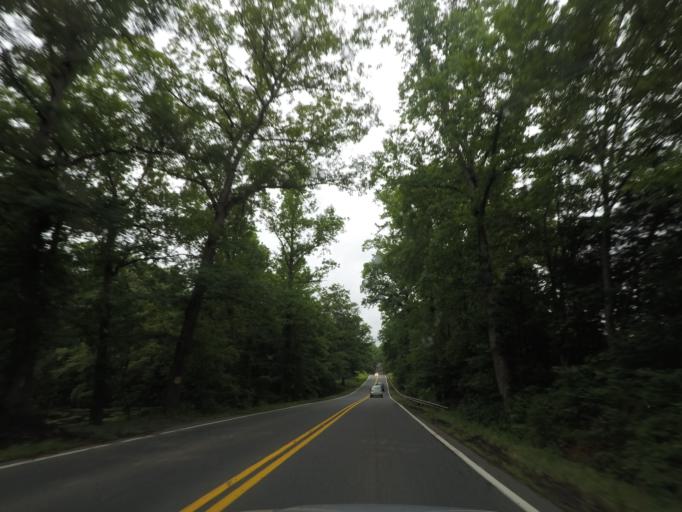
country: US
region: Virginia
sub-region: Fluvanna County
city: Palmyra
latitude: 37.9439
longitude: -78.2433
